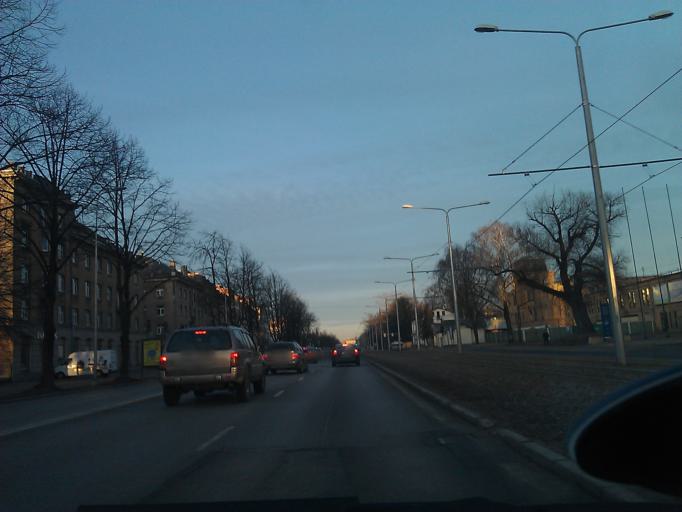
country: LV
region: Riga
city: Bergi
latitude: 56.9886
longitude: 24.2343
